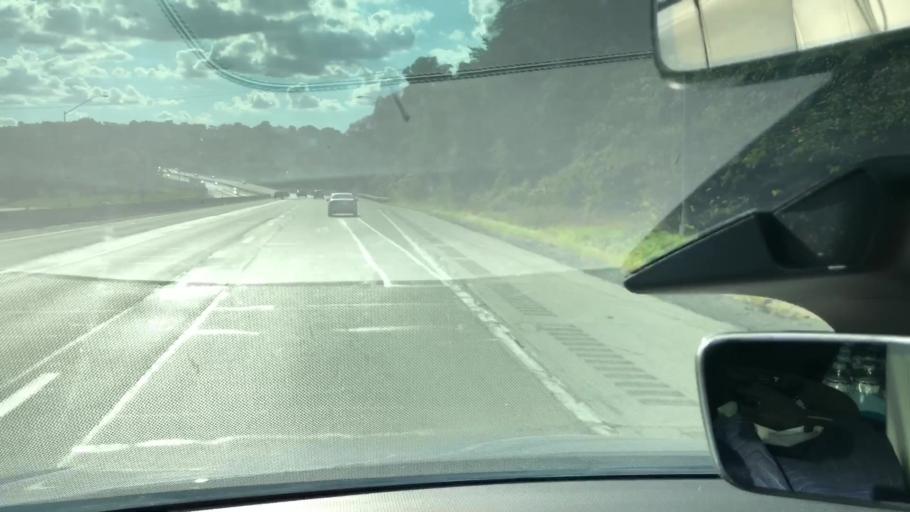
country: US
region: Pennsylvania
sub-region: Allegheny County
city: Churchill
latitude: 40.4425
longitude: -79.8234
